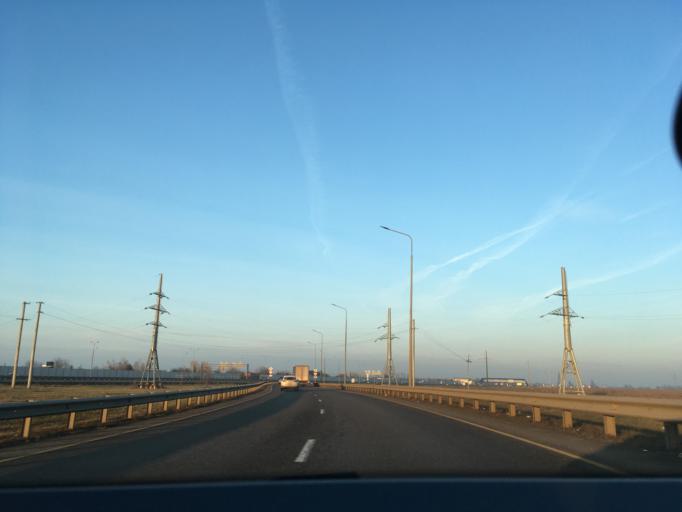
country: RU
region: Krasnodarskiy
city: Agronom
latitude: 45.1802
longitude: 39.1139
